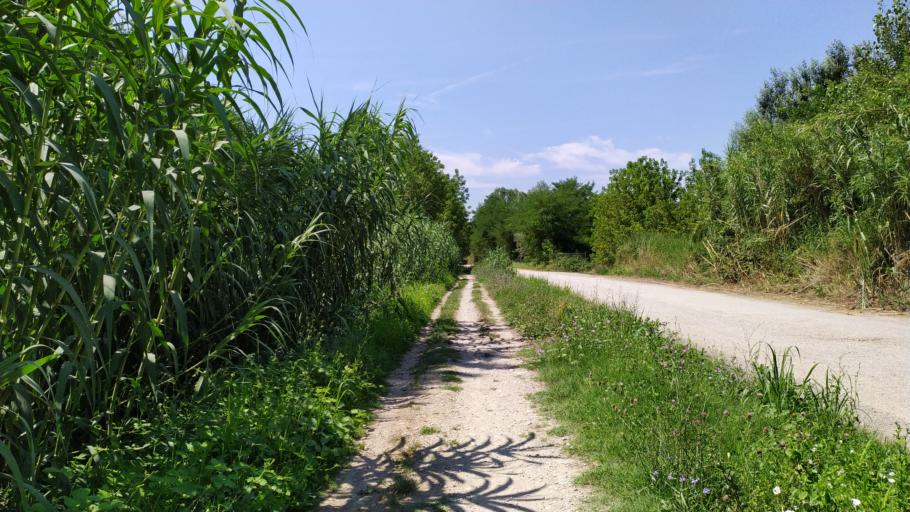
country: IT
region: Emilia-Romagna
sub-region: Forli-Cesena
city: Forli
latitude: 44.2064
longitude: 12.0107
